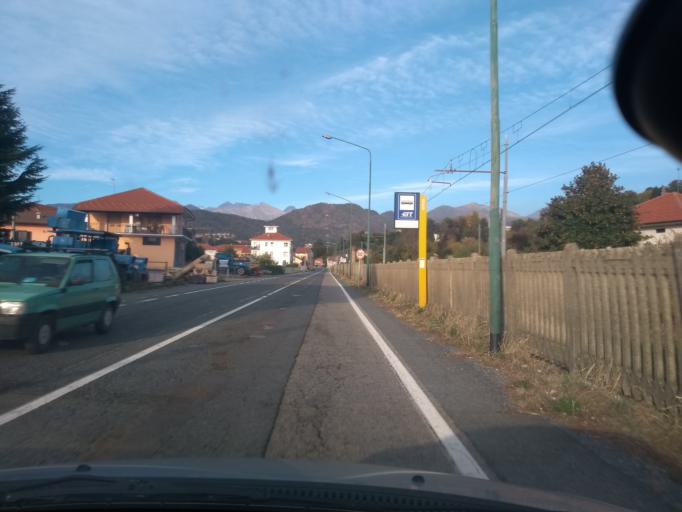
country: IT
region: Piedmont
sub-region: Provincia di Torino
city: Lanzo Torinese
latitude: 45.2719
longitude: 7.4930
